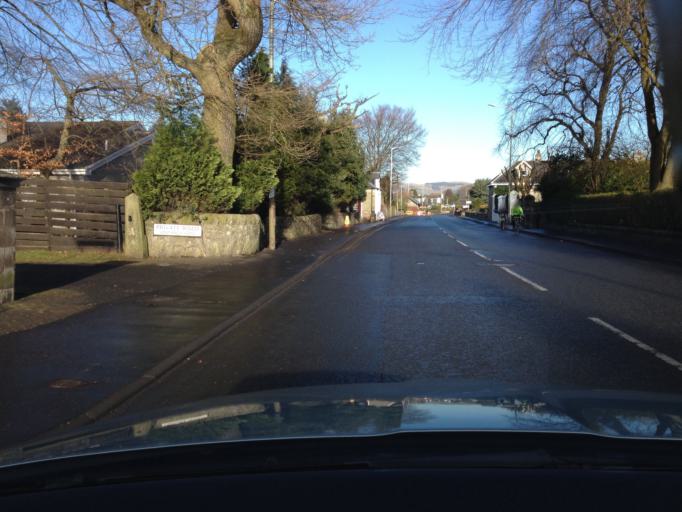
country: GB
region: Scotland
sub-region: Perth and Kinross
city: Kinross
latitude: 56.2122
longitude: -3.4262
